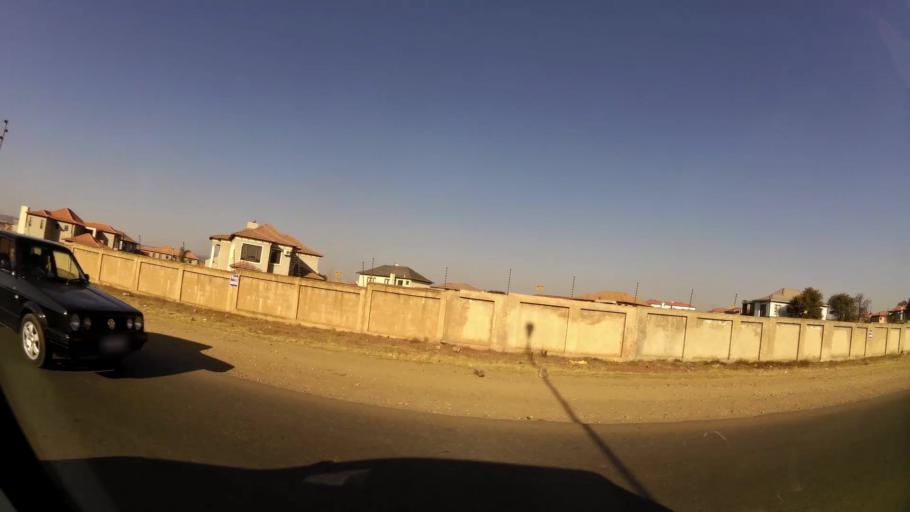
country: ZA
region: Gauteng
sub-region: City of Tshwane Metropolitan Municipality
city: Pretoria
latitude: -25.7554
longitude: 28.3656
